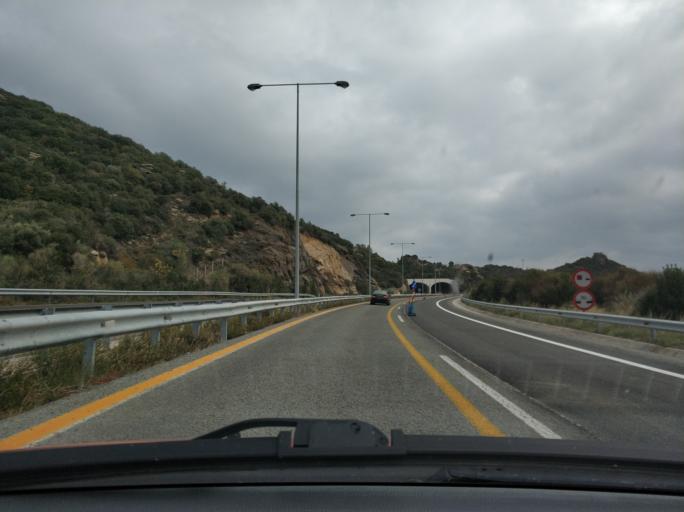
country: GR
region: East Macedonia and Thrace
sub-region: Nomos Kavalas
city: Palaio Tsifliki
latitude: 40.9102
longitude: 24.3521
